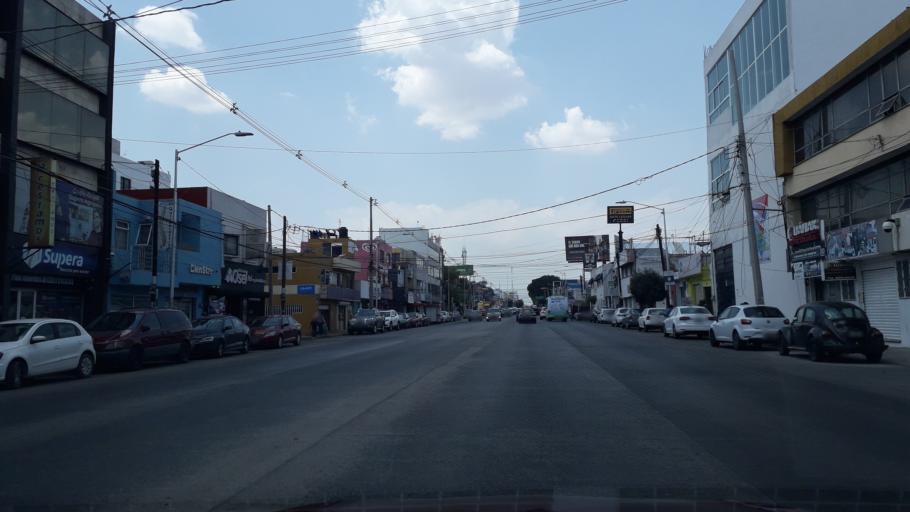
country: MX
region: Puebla
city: Puebla
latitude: 19.0352
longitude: -98.2105
